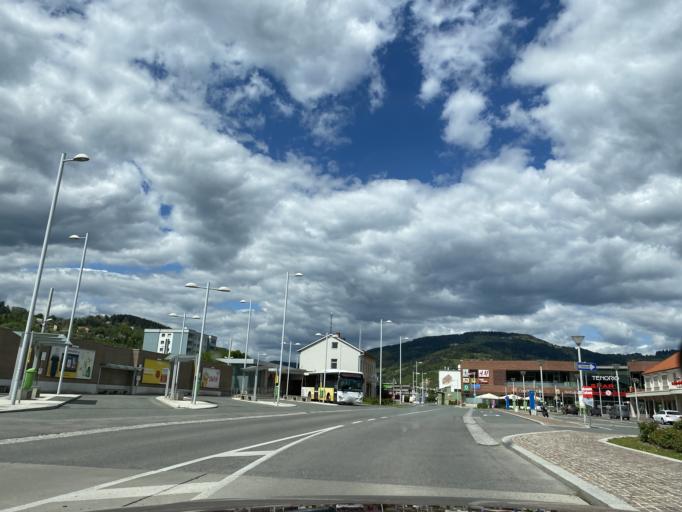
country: AT
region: Carinthia
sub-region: Politischer Bezirk Wolfsberg
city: Wolfsberg
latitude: 46.8411
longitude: 14.8389
